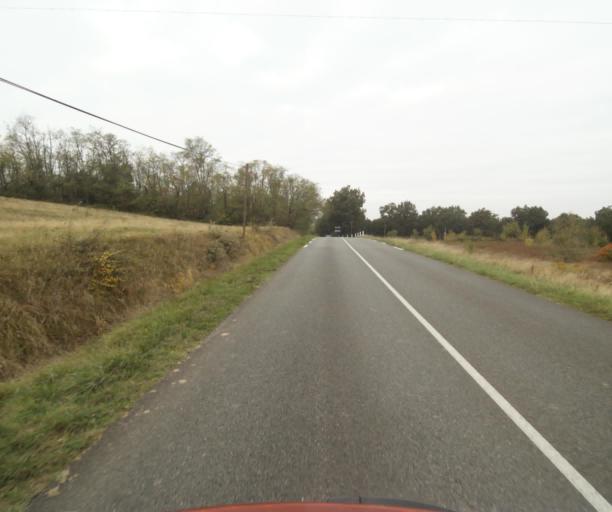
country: FR
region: Midi-Pyrenees
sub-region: Departement du Tarn-et-Garonne
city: Verdun-sur-Garonne
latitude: 43.7965
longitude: 1.2290
